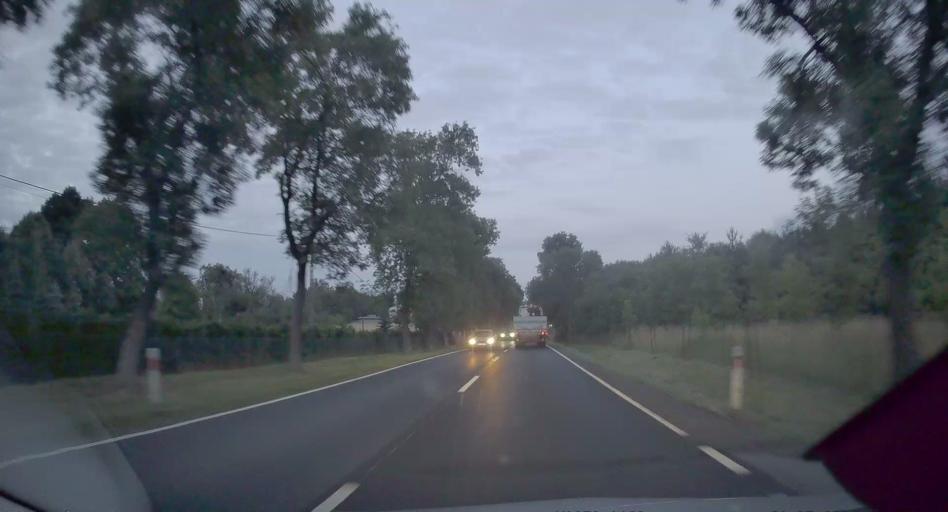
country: PL
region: Silesian Voivodeship
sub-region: Powiat klobucki
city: Opatow
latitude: 50.9572
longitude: 18.7860
